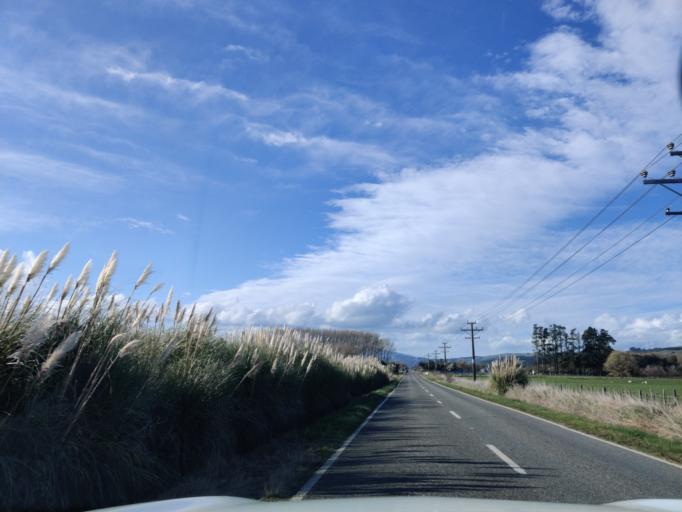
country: NZ
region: Manawatu-Wanganui
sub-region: Palmerston North City
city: Palmerston North
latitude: -40.3553
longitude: 175.6888
